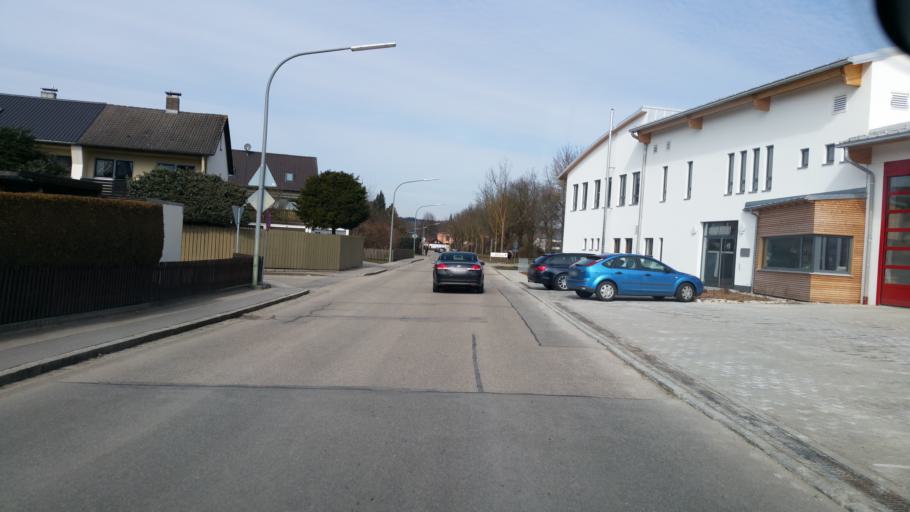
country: DE
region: Bavaria
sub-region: Lower Bavaria
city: Tiefenbach
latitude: 48.5507
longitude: 12.1080
